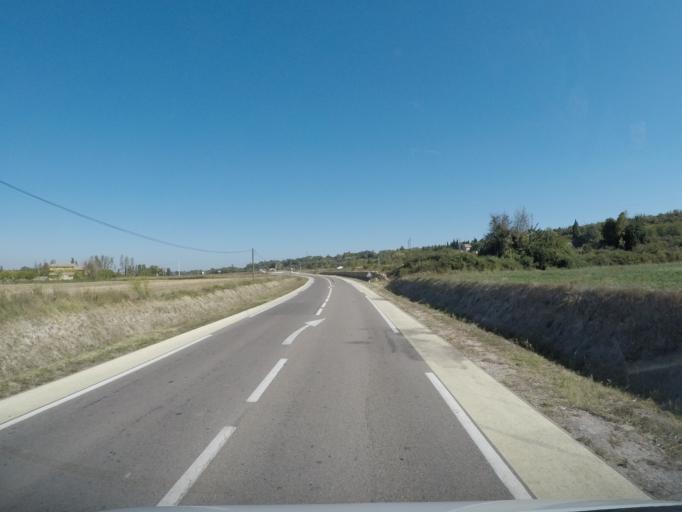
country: FR
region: Languedoc-Roussillon
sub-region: Departement du Gard
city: Uzes
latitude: 44.0017
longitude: 4.4006
